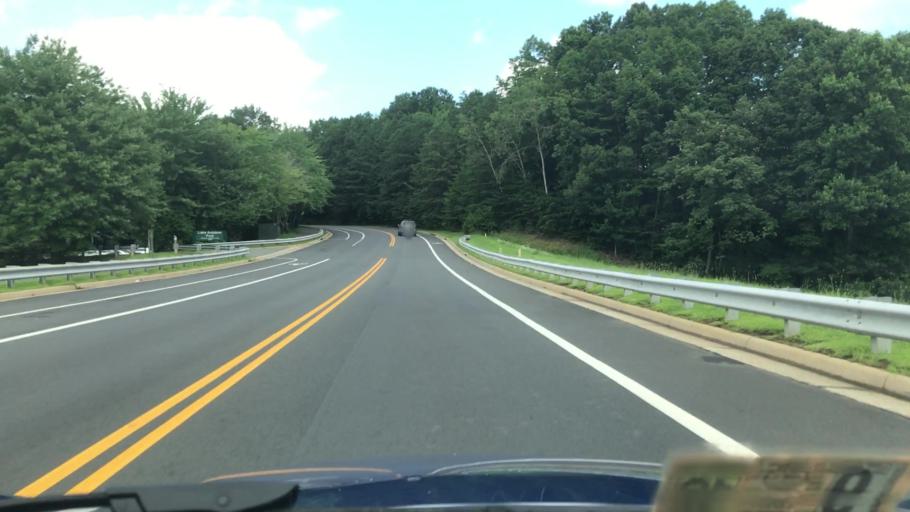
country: US
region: Virginia
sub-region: Fairfax County
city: Reston
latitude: 38.9326
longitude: -77.3251
